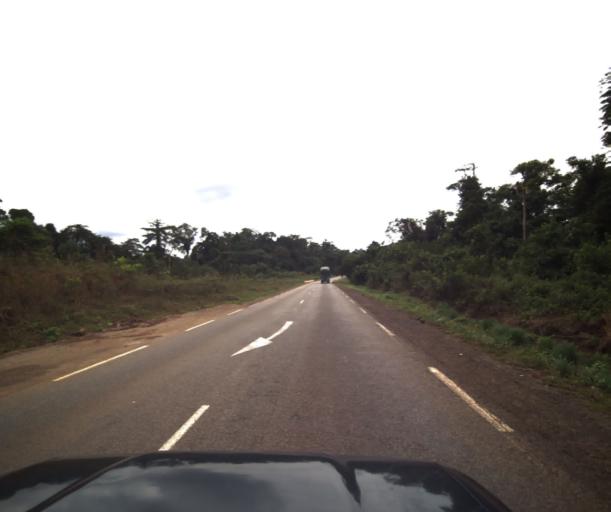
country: CM
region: Littoral
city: Edea
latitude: 3.8315
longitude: 10.4017
